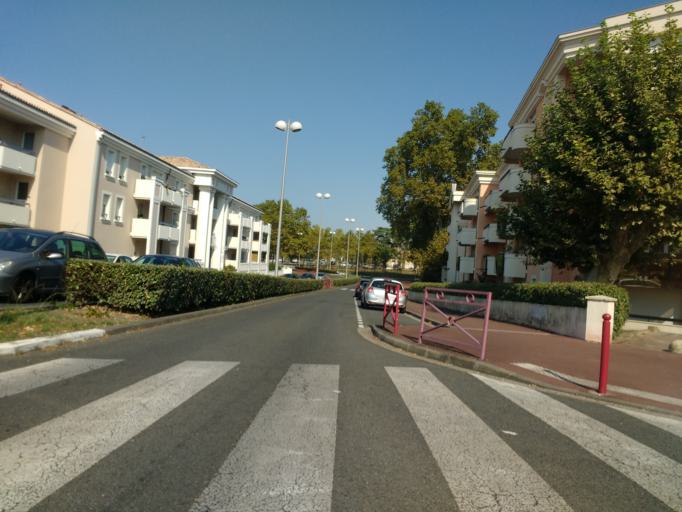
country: FR
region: Aquitaine
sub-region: Departement de la Gironde
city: Pessac
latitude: 44.8100
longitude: -0.6294
